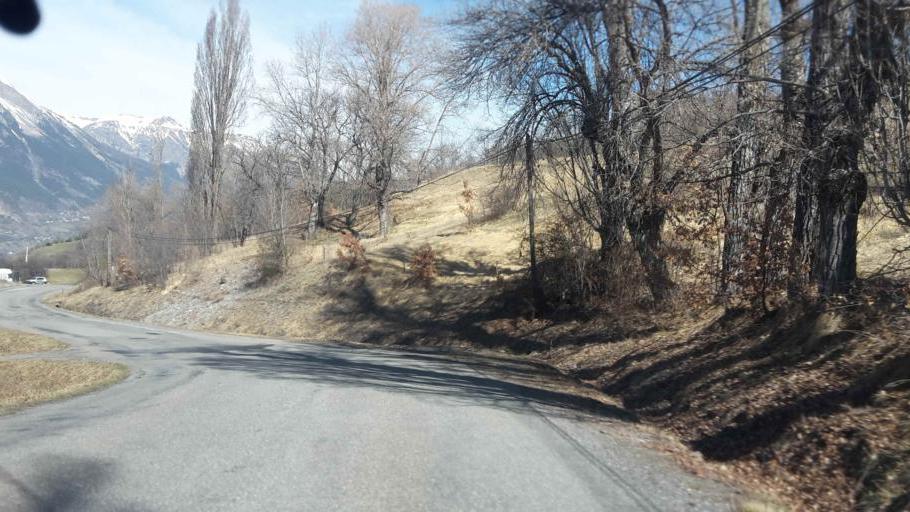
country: FR
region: Provence-Alpes-Cote d'Azur
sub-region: Departement des Hautes-Alpes
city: Embrun
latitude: 44.5695
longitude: 6.5353
